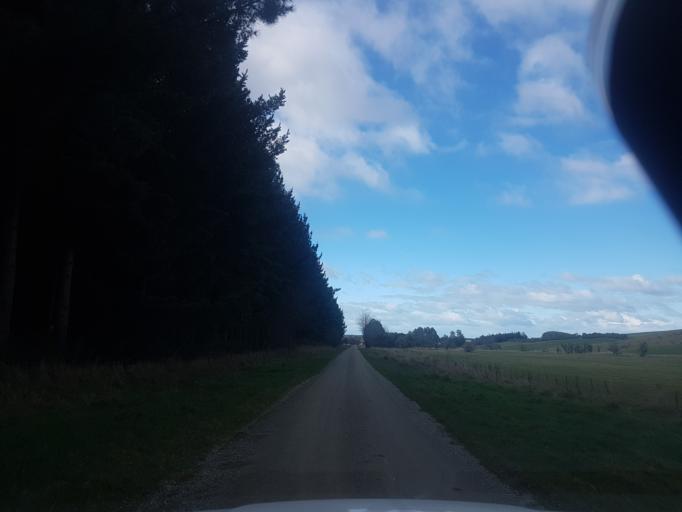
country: NZ
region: Canterbury
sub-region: Timaru District
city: Pleasant Point
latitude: -44.1879
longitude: 171.1634
